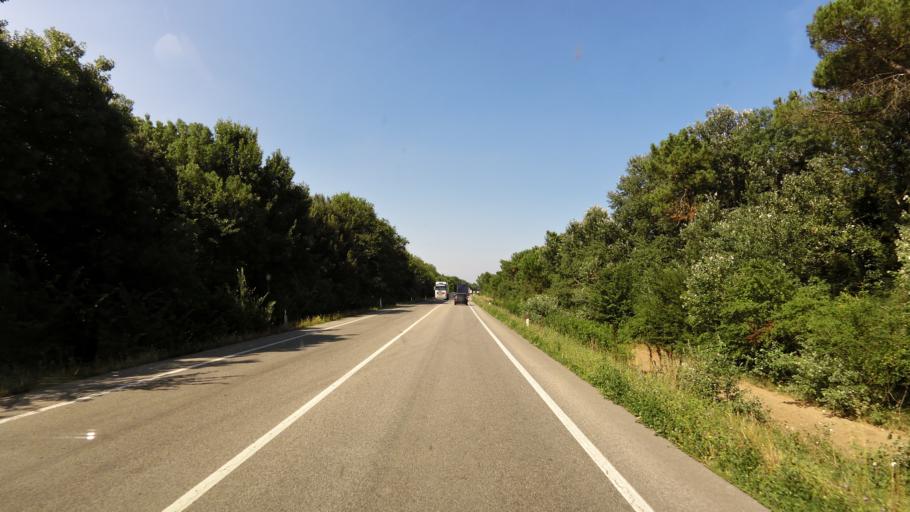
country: IT
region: Emilia-Romagna
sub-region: Provincia di Ravenna
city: Marina Romea
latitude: 44.4958
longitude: 12.2166
